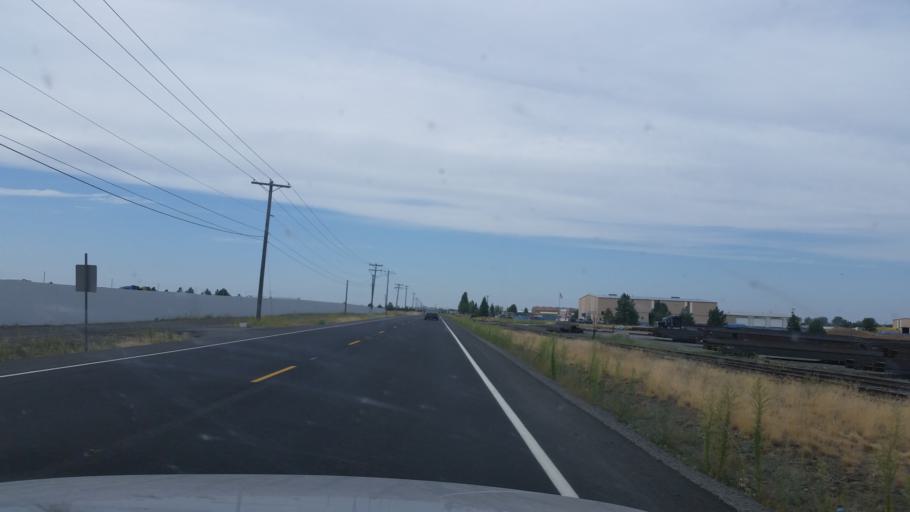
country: US
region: Washington
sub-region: Spokane County
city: Airway Heights
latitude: 47.6284
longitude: -117.5645
